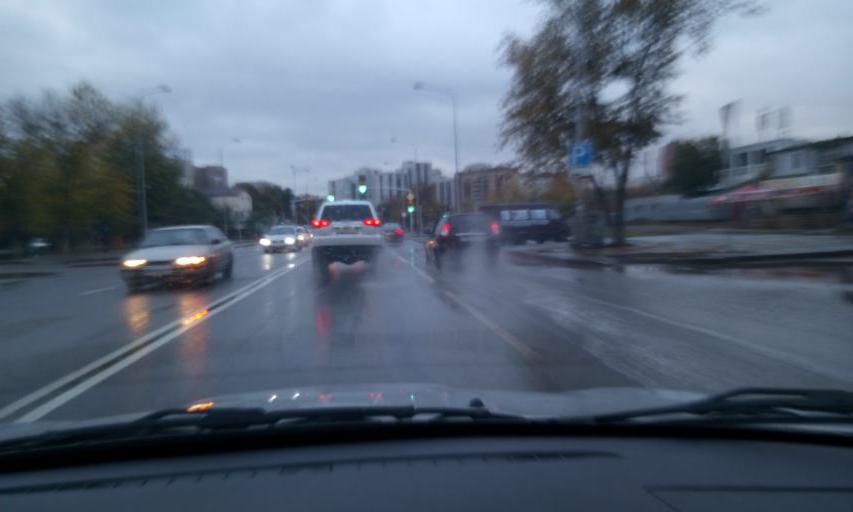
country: KZ
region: Astana Qalasy
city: Astana
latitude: 51.1634
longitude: 71.4513
